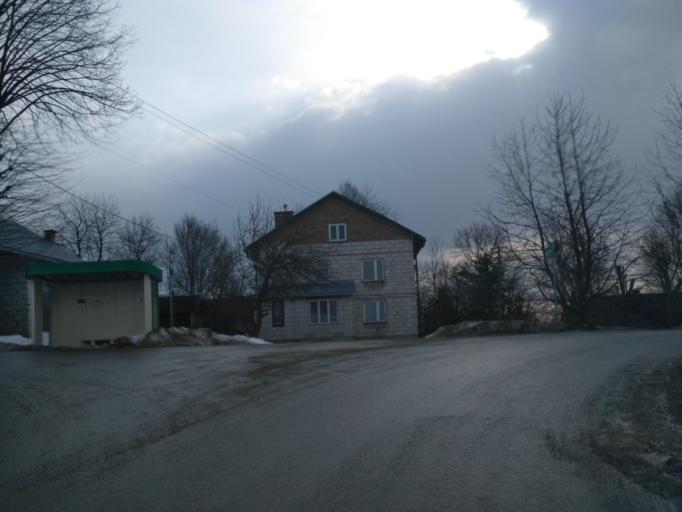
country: PL
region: Subcarpathian Voivodeship
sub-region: Powiat brzozowski
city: Dydnia
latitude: 49.6486
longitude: 22.1612
